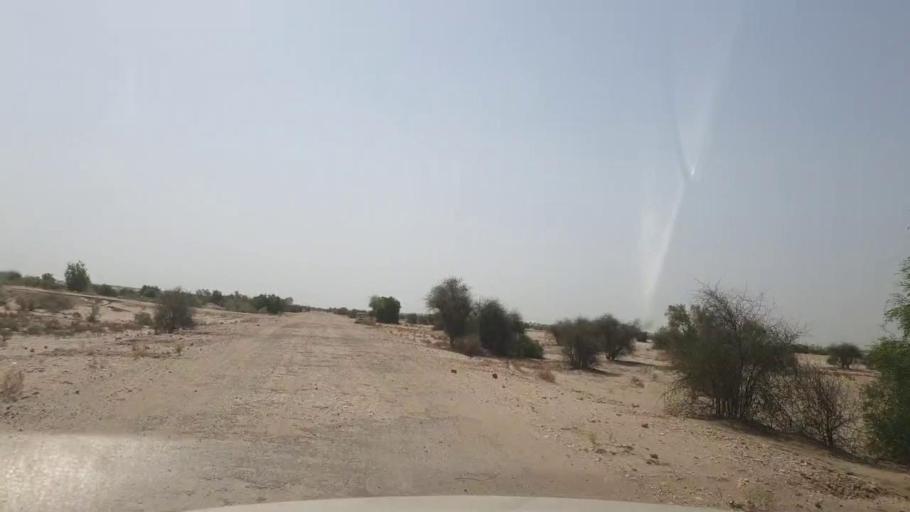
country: PK
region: Sindh
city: Rohri
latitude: 27.4485
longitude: 69.2321
